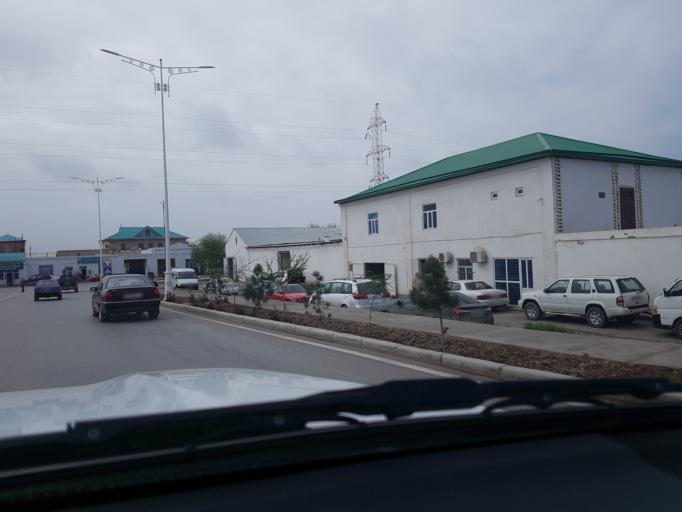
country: TM
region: Lebap
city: Turkmenabat
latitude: 39.0733
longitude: 63.5950
